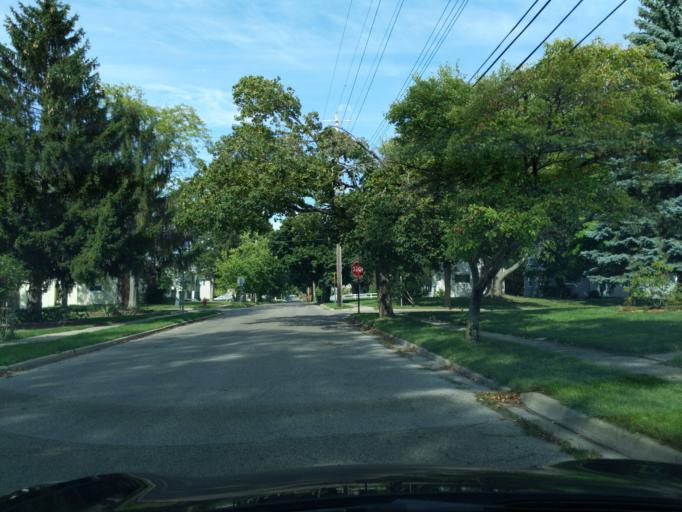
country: US
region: Michigan
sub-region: Ingham County
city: Lansing
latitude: 42.7046
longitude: -84.5419
